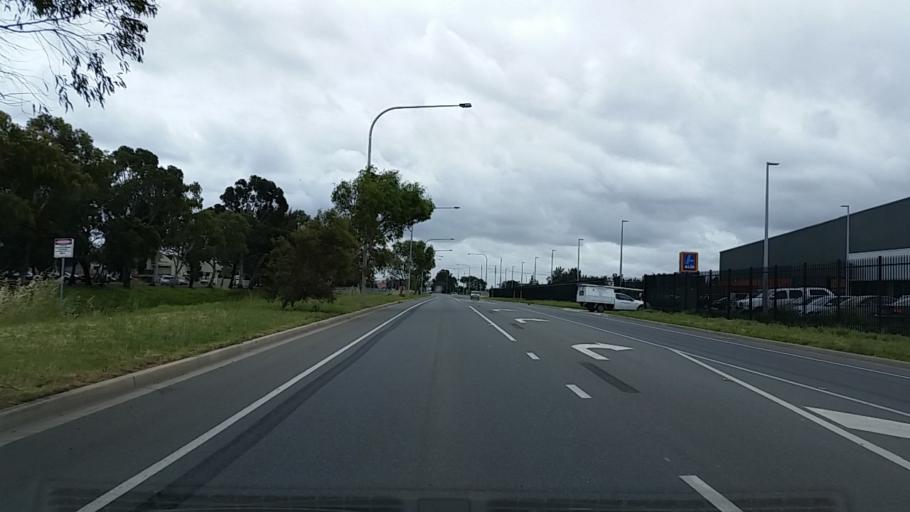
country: AU
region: South Australia
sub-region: Port Adelaide Enfield
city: Blair Athol
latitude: -34.8532
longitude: 138.5742
